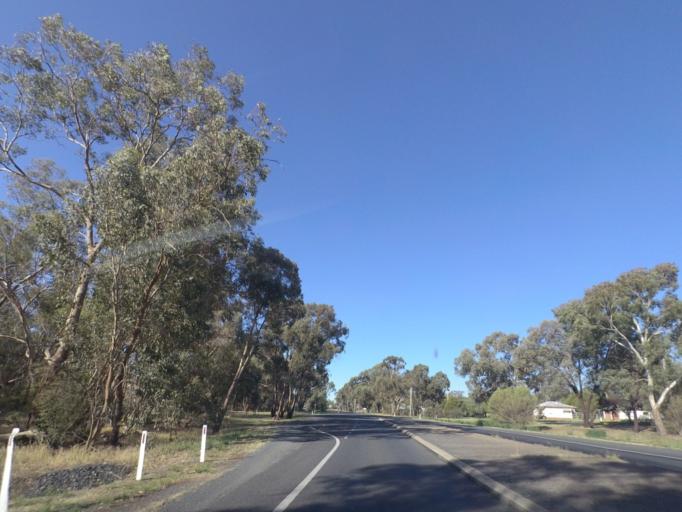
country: AU
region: New South Wales
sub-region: Wagga Wagga
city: Forest Hill
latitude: -35.2740
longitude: 147.7412
